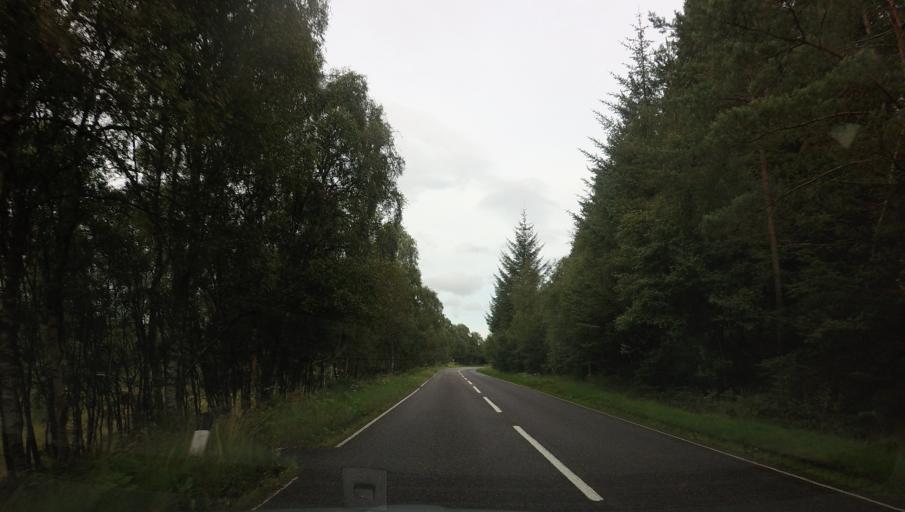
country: GB
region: Scotland
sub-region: Aberdeenshire
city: Torphins
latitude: 57.0642
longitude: -2.5920
